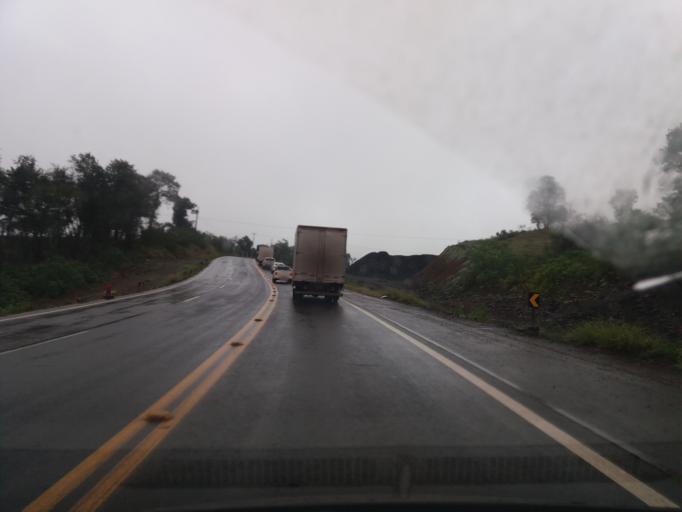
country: BR
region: Parana
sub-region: Realeza
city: Realeza
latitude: -25.4737
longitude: -53.5874
